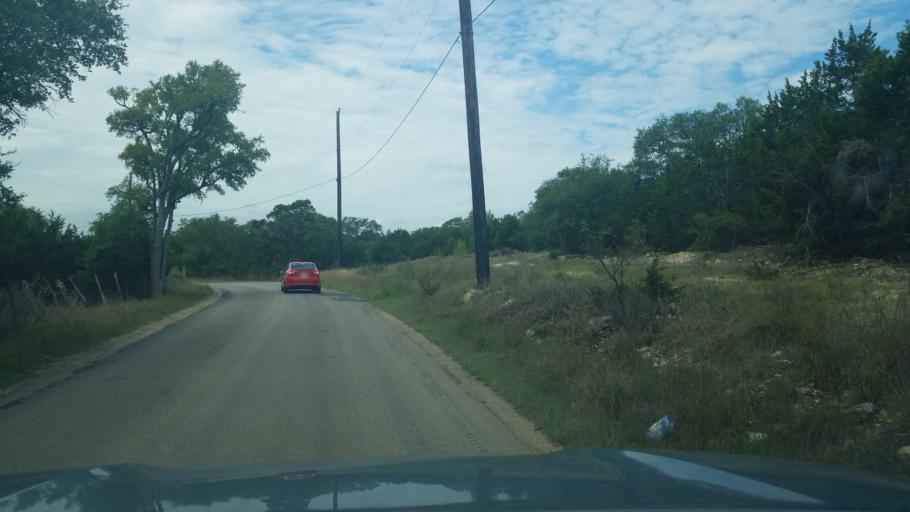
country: US
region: Texas
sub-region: Comal County
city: Bulverde
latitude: 29.7741
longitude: -98.4133
